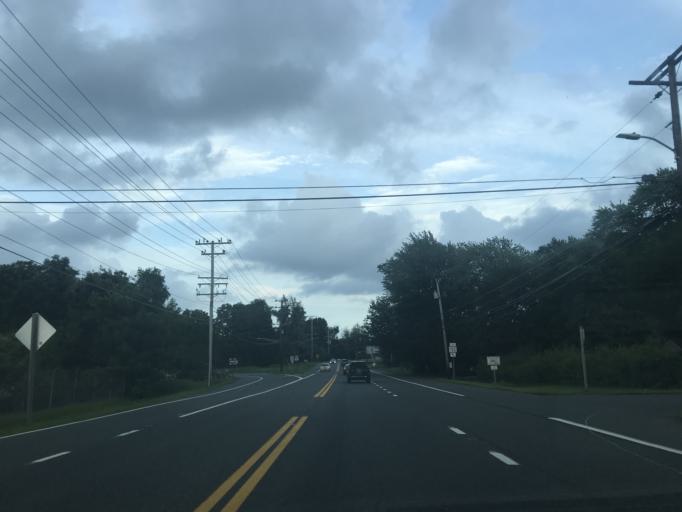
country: US
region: Maryland
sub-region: Harford County
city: Riverside
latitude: 39.5550
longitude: -76.2392
